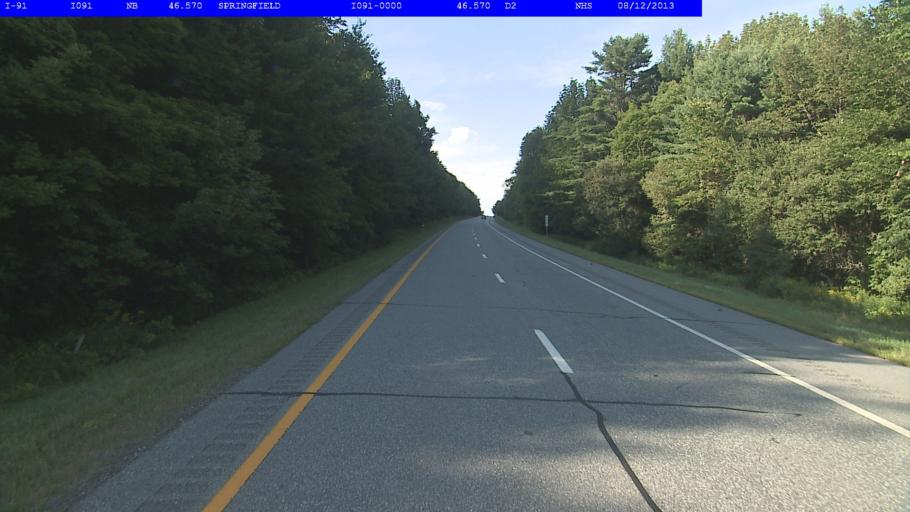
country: US
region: Vermont
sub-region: Windsor County
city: Springfield
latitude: 43.3351
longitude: -72.4197
